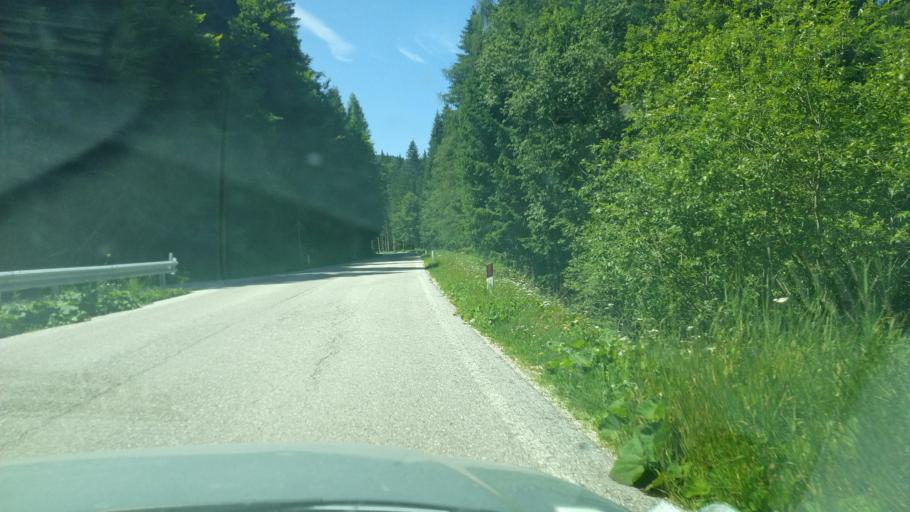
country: IT
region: Trentino-Alto Adige
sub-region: Provincia di Trento
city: Folgaria
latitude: 45.9063
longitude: 11.2161
